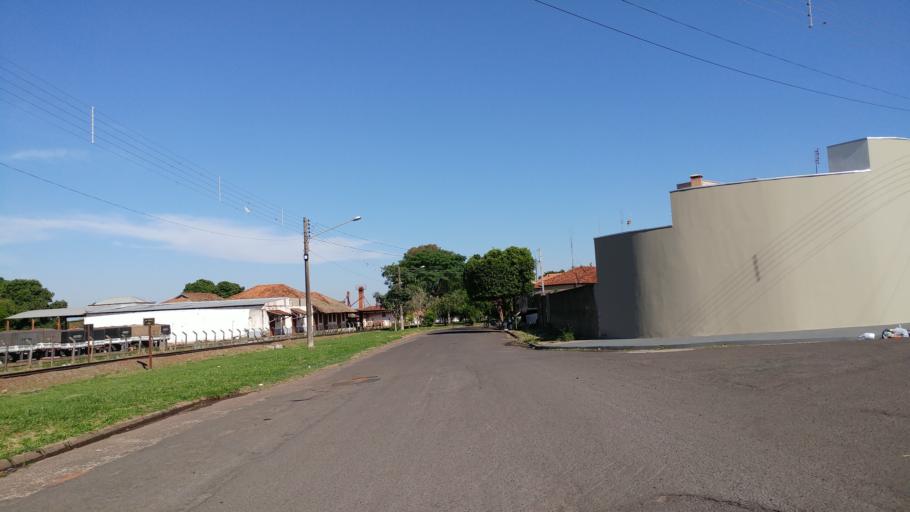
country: BR
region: Sao Paulo
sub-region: Paraguacu Paulista
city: Paraguacu Paulista
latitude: -22.4079
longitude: -50.5733
